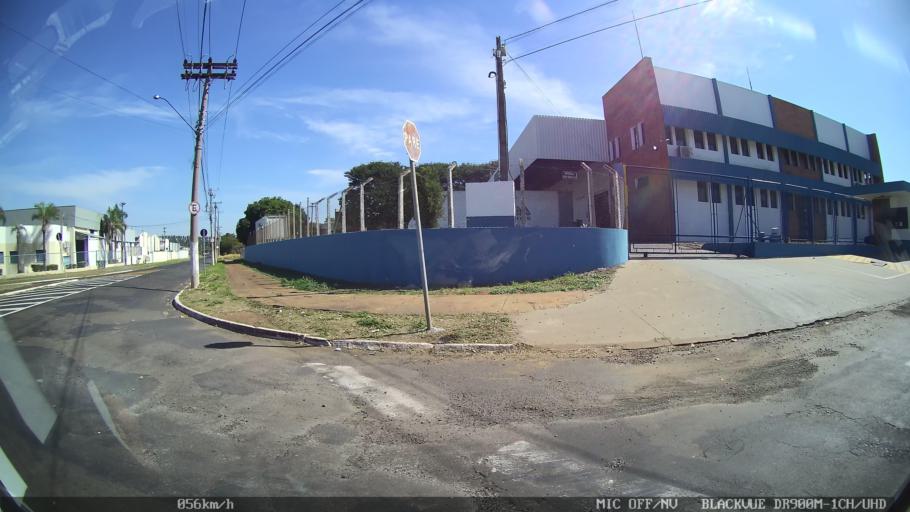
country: BR
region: Sao Paulo
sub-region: Franca
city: Franca
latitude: -20.5534
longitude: -47.4372
